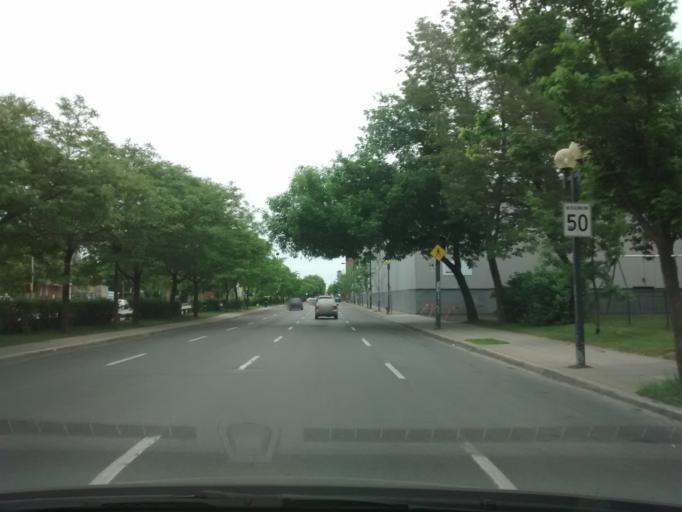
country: CA
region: Quebec
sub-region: Monteregie
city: Longueuil
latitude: 45.5337
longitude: -73.5562
